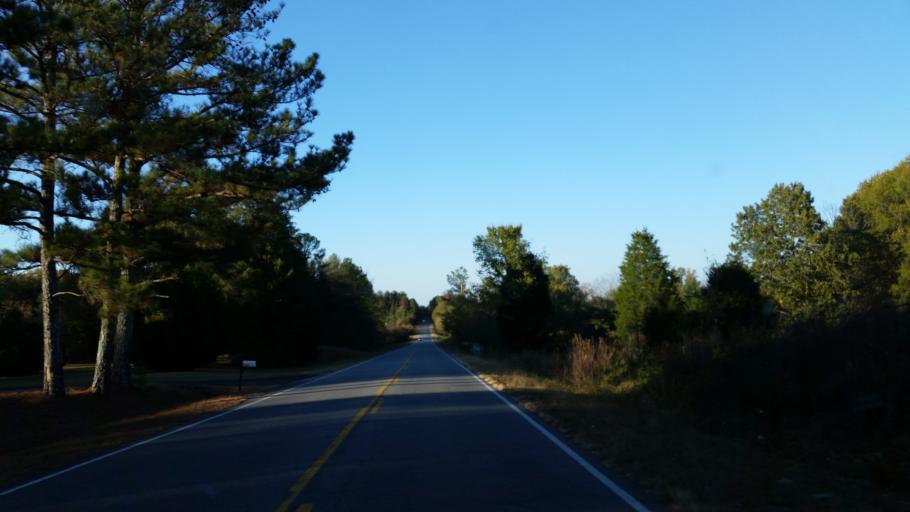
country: US
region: Georgia
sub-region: Bartow County
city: Adairsville
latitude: 34.3494
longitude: -84.9387
